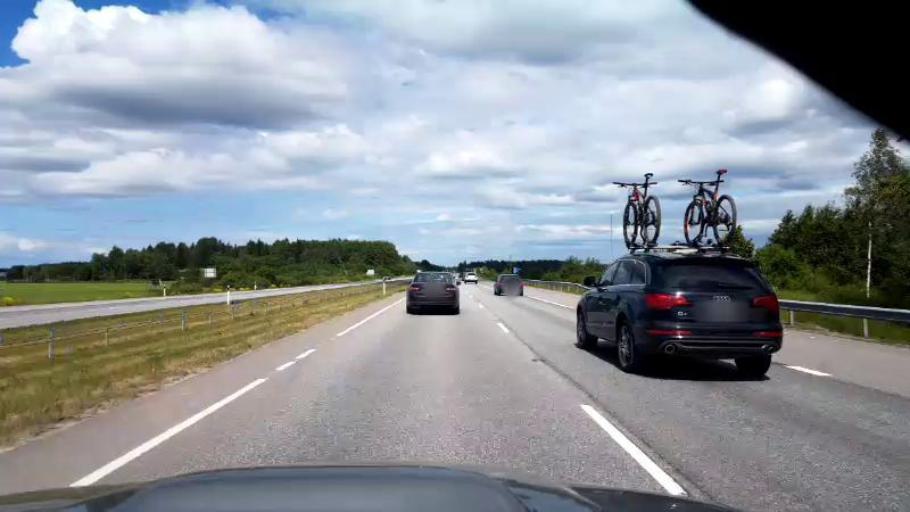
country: EE
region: Harju
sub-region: Saue linn
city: Saue
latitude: 59.2803
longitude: 24.5288
